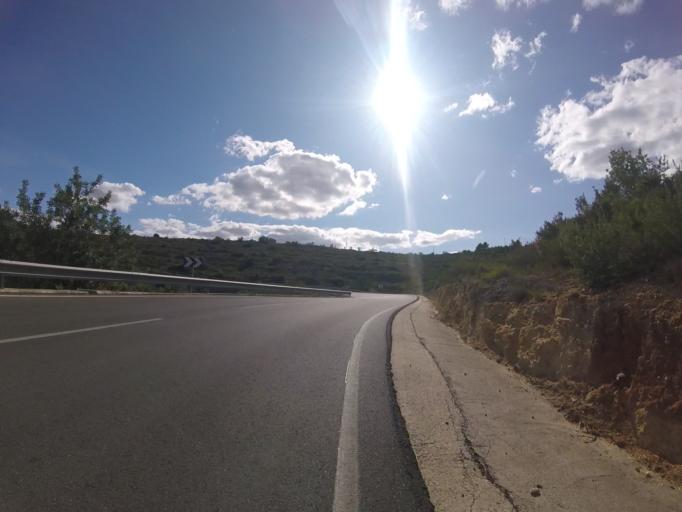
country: ES
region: Valencia
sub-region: Provincia de Castello
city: Cuevas de Vinroma
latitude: 40.3153
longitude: 0.1342
